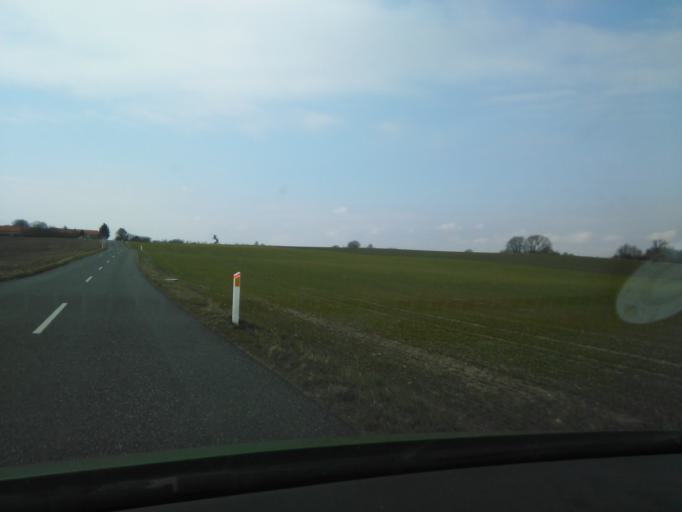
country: DK
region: Central Jutland
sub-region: Arhus Kommune
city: Beder
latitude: 56.0612
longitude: 10.2315
